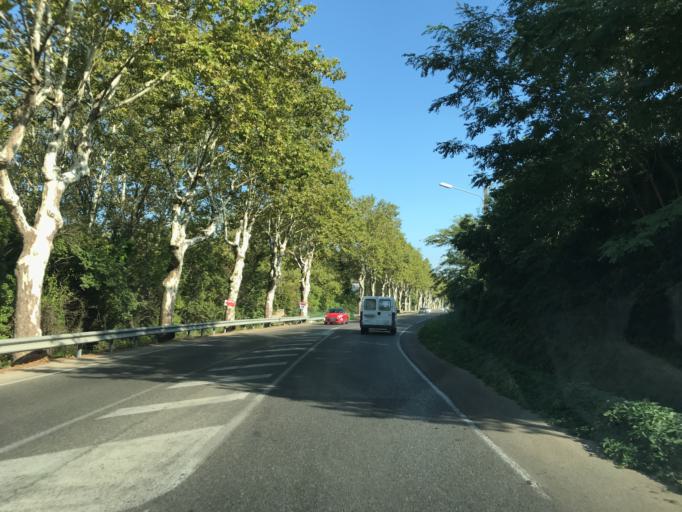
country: FR
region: Provence-Alpes-Cote d'Azur
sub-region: Departement des Bouches-du-Rhone
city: Miramas
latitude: 43.5701
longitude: 5.0212
